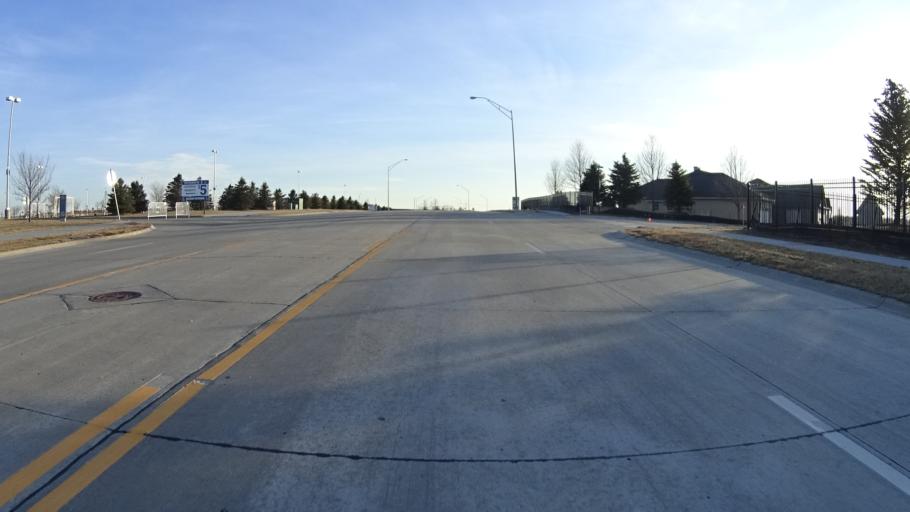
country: US
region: Nebraska
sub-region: Sarpy County
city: Chalco
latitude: 41.1526
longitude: -96.1099
